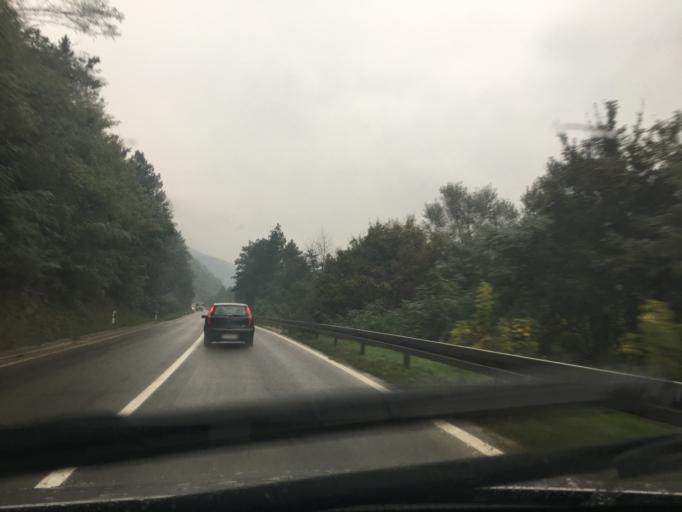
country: RS
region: Central Serbia
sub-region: Pcinjski Okrug
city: Vladicin Han
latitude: 42.7590
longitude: 22.0839
